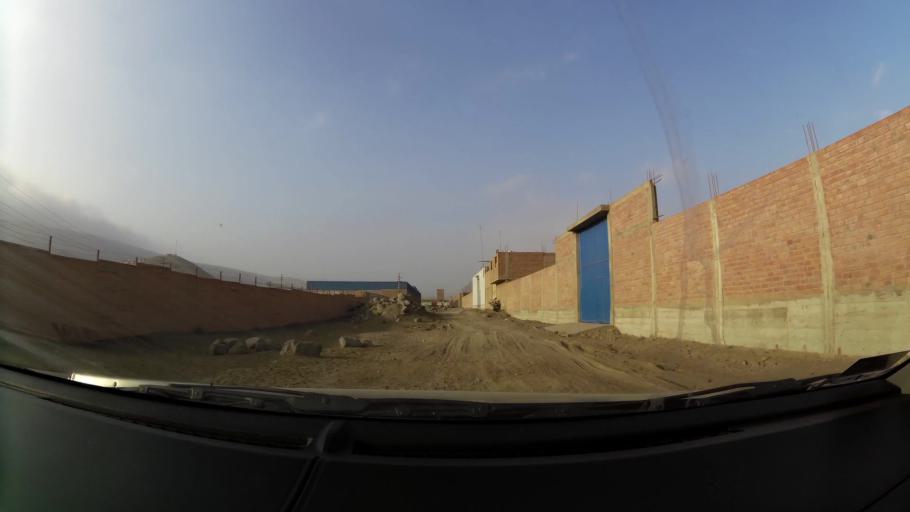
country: PE
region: Lima
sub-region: Lima
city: Santa Rosa
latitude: -11.7513
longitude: -77.1504
